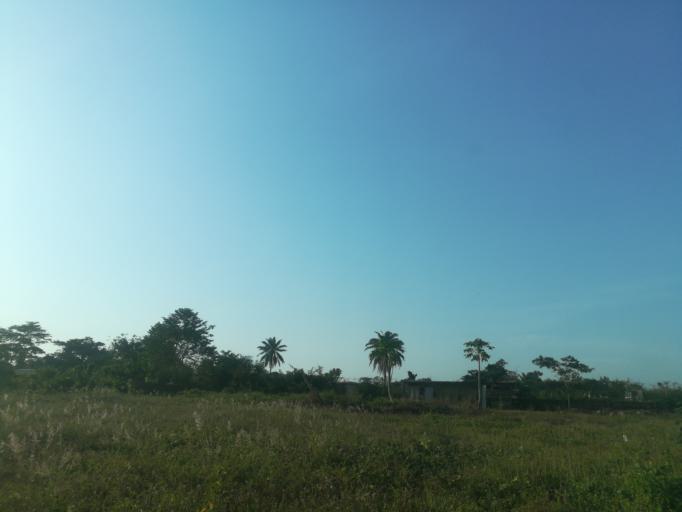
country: NG
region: Oyo
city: Moniya
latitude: 7.5491
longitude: 3.8919
